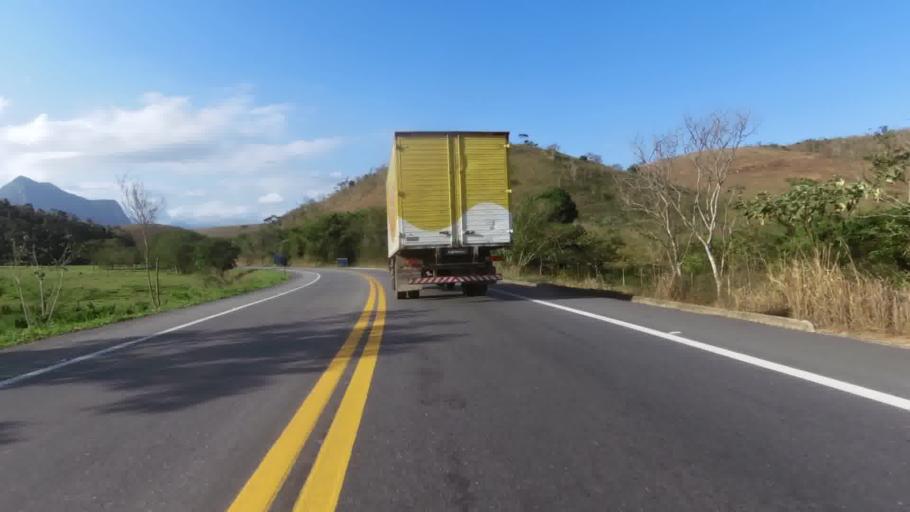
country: BR
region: Espirito Santo
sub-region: Mimoso Do Sul
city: Mimoso do Sul
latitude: -21.1666
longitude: -41.2866
